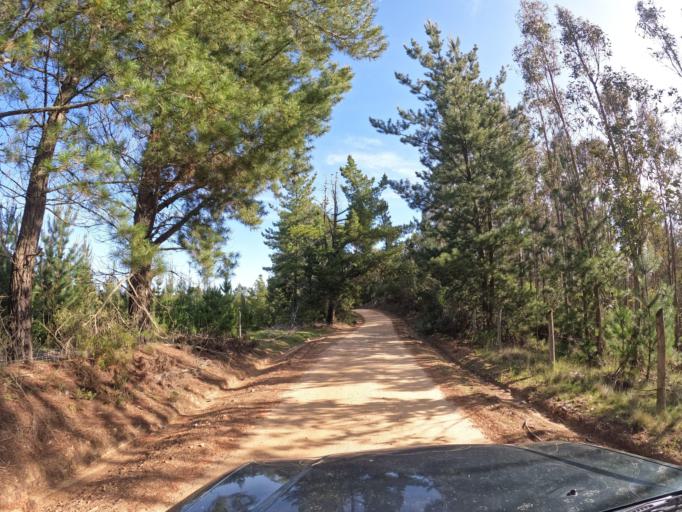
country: CL
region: Biobio
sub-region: Provincia de Biobio
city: La Laja
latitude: -37.1182
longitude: -72.7377
